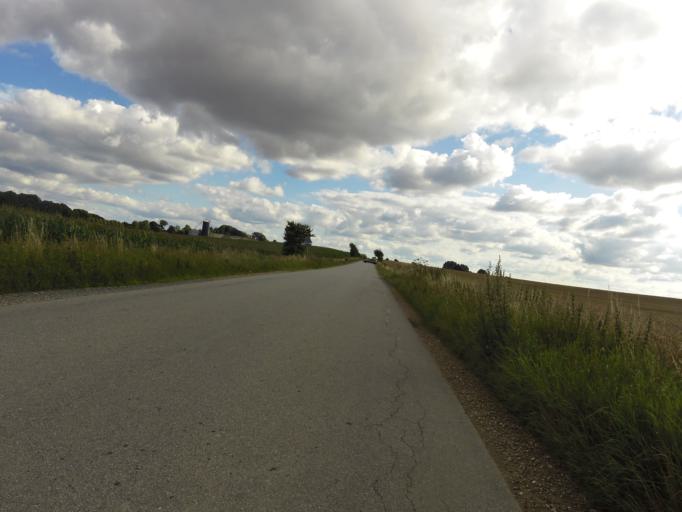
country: DK
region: South Denmark
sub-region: Haderslev Kommune
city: Haderslev
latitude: 55.2194
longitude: 9.4444
